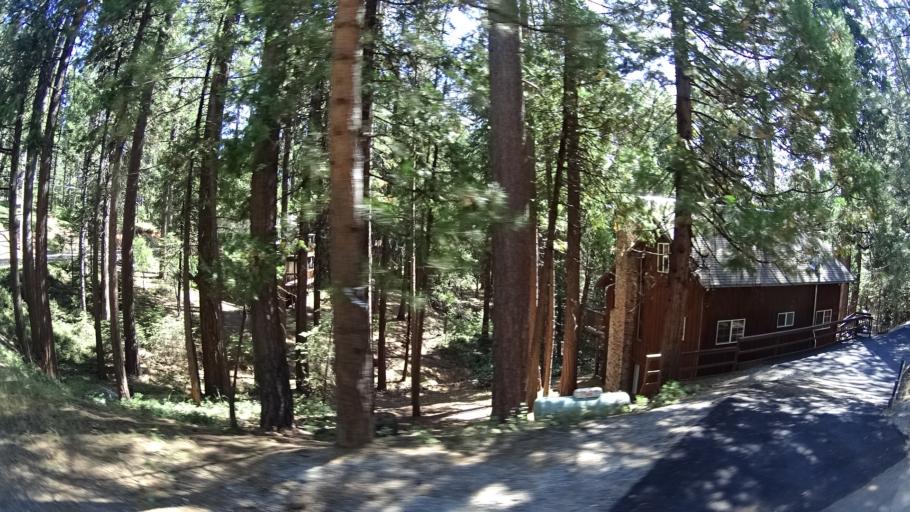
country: US
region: California
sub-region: Calaveras County
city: Arnold
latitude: 38.2496
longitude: -120.3676
